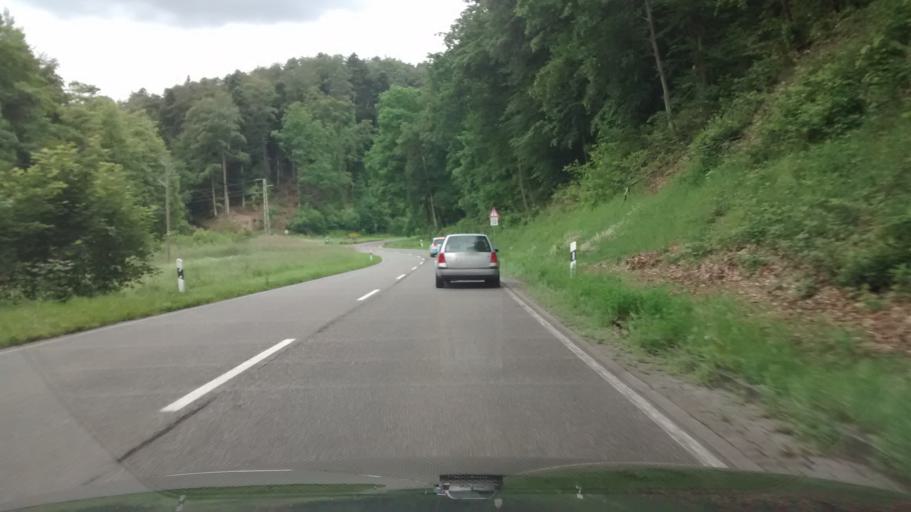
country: DE
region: Rheinland-Pfalz
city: Dorrenbach
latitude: 49.1075
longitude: 7.9698
